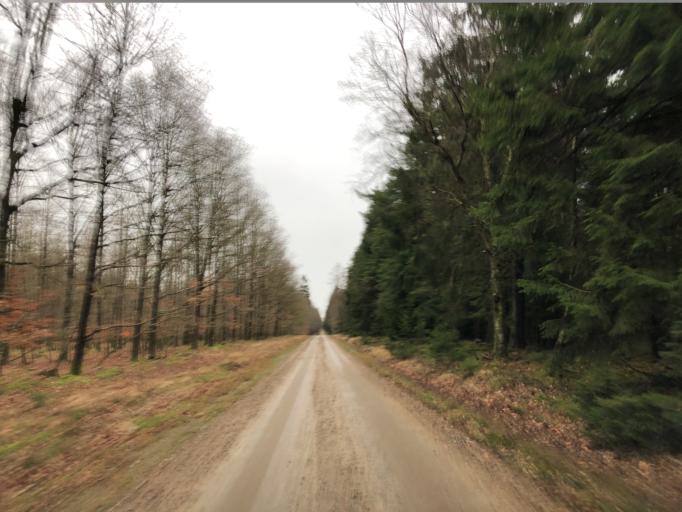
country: DK
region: Central Jutland
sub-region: Holstebro Kommune
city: Vinderup
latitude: 56.3872
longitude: 8.8676
